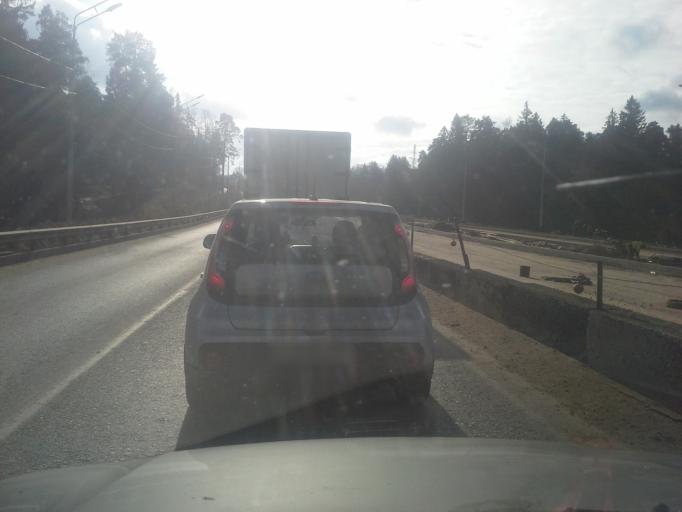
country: RU
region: Moskovskaya
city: Zvenigorod
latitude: 55.7108
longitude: 36.8737
